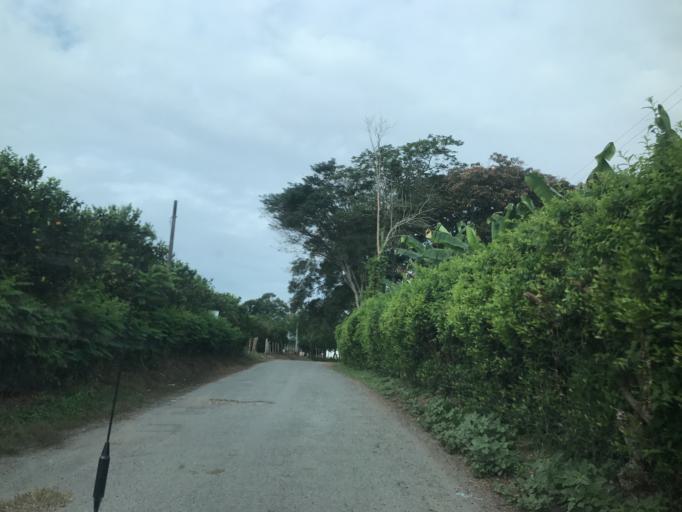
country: CO
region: Quindio
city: Montenegro
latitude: 4.5410
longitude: -75.8535
